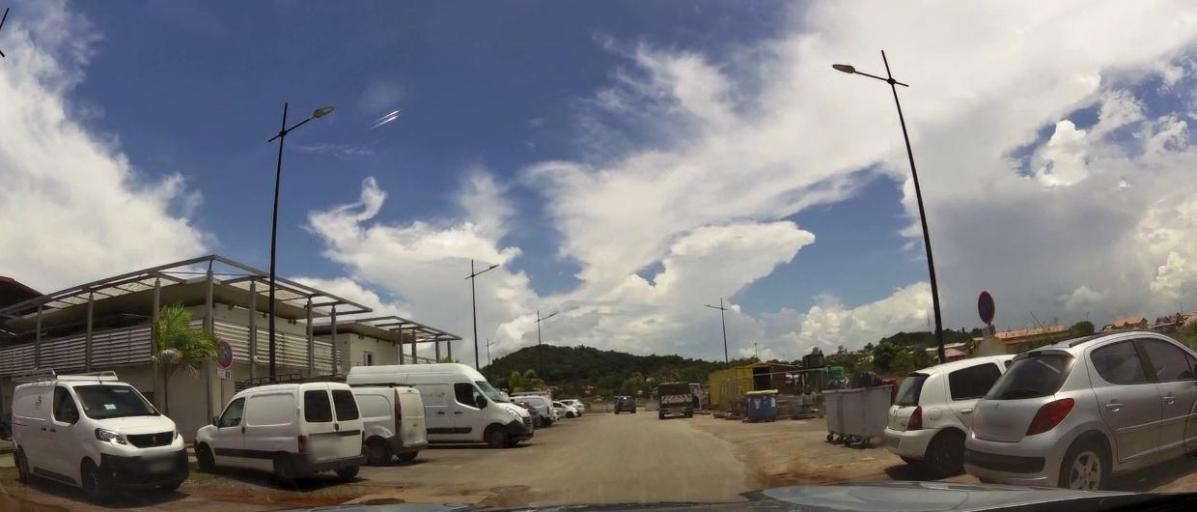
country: GF
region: Guyane
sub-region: Guyane
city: Cayenne
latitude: 4.9319
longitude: -52.3027
